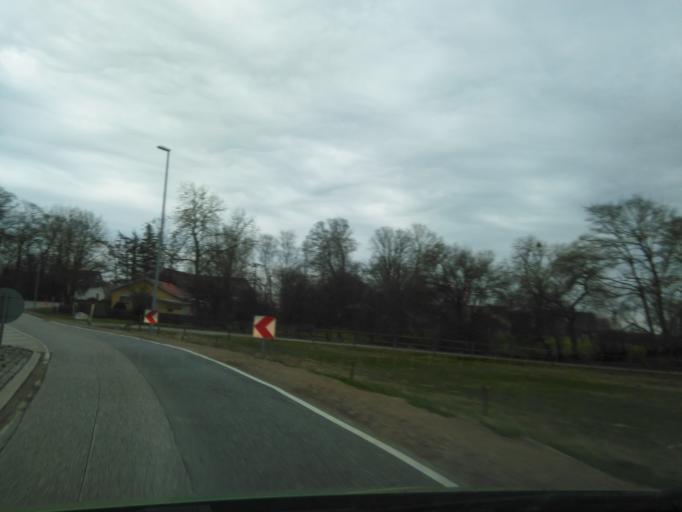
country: DK
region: Central Jutland
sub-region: Randers Kommune
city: Spentrup
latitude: 56.5573
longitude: 10.0011
